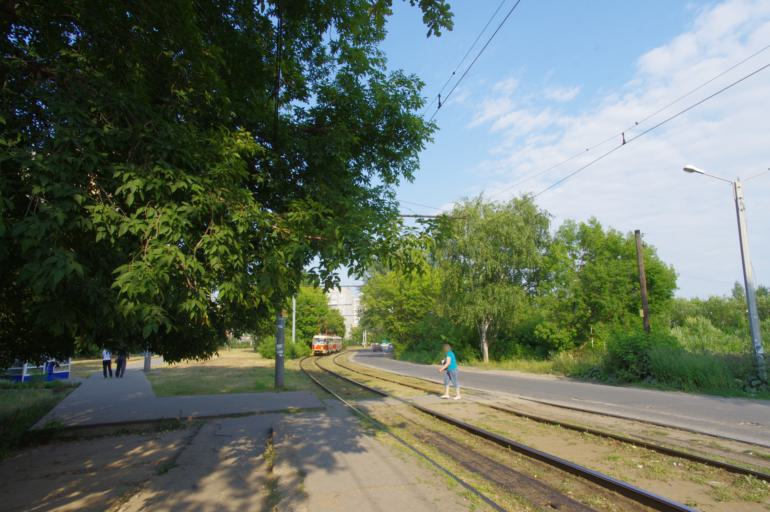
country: RU
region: Nizjnij Novgorod
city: Nizhniy Novgorod
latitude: 56.3352
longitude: 43.9169
